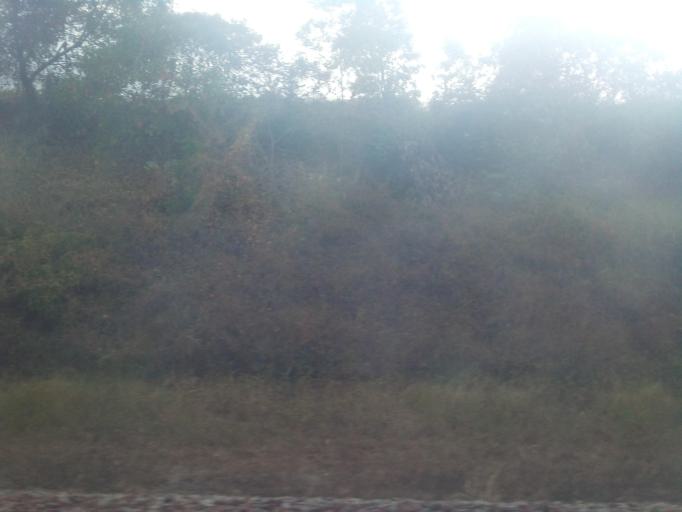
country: BR
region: Maranhao
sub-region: Sao Luis
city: Sao Luis
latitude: -2.6444
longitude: -44.3048
